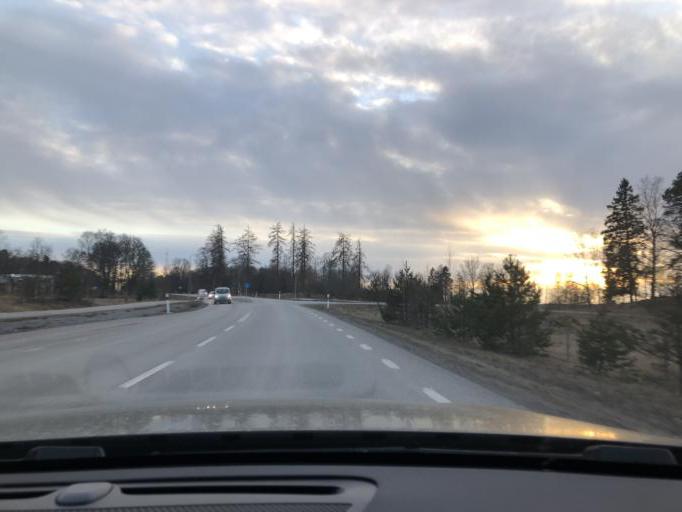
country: SE
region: Uppsala
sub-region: Uppsala Kommun
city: Gamla Uppsala
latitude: 59.9385
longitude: 17.6508
